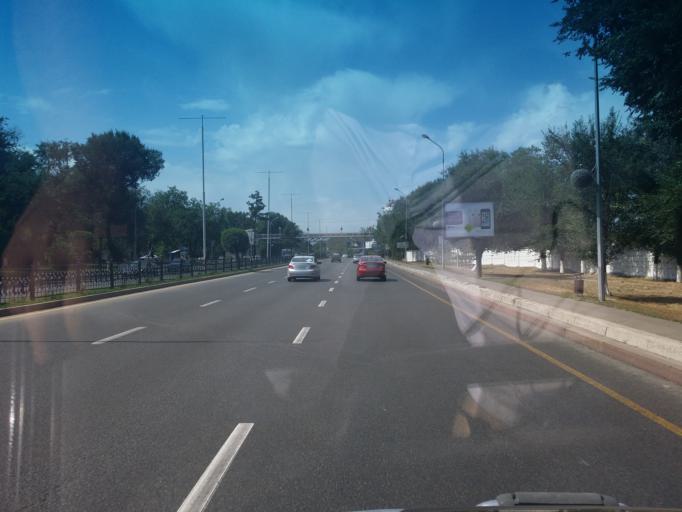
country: KZ
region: Almaty Qalasy
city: Almaty
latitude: 43.1993
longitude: 76.9020
